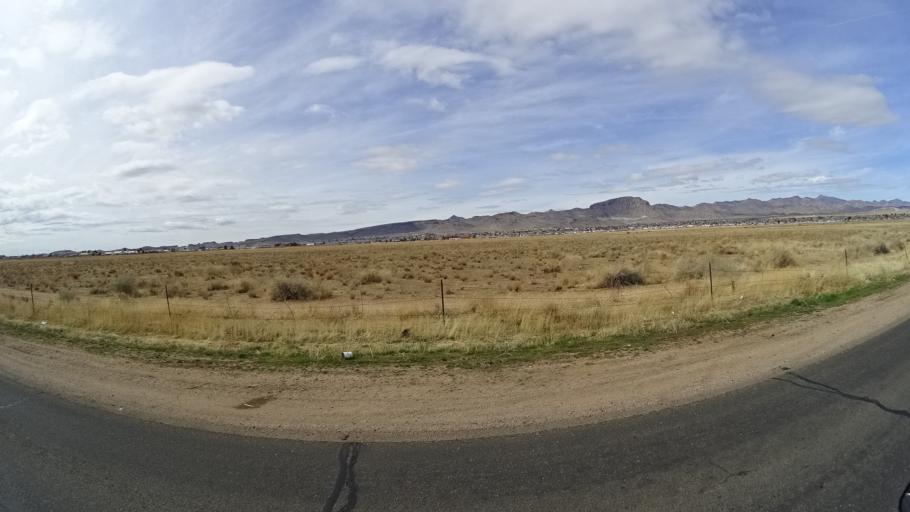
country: US
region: Arizona
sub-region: Mohave County
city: New Kingman-Butler
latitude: 35.2429
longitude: -113.9941
